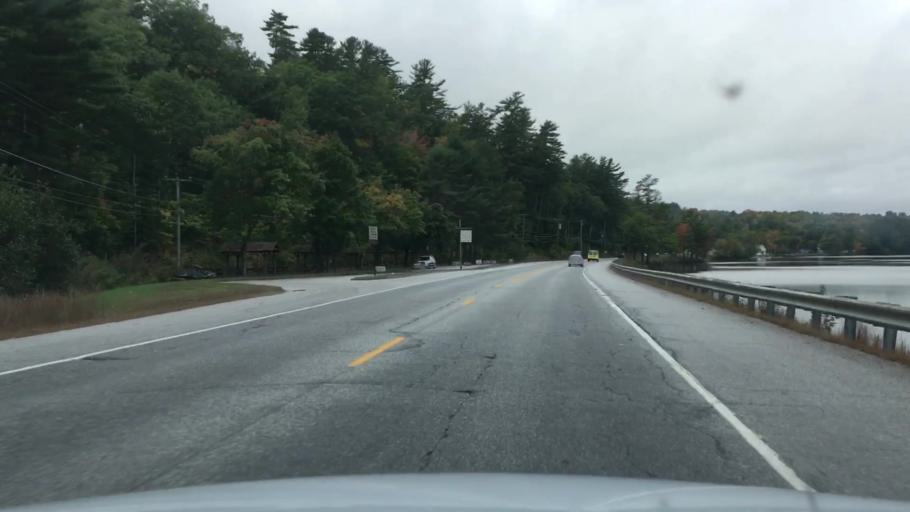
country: US
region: Maine
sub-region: Oxford County
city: Norway
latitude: 44.2121
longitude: -70.5658
